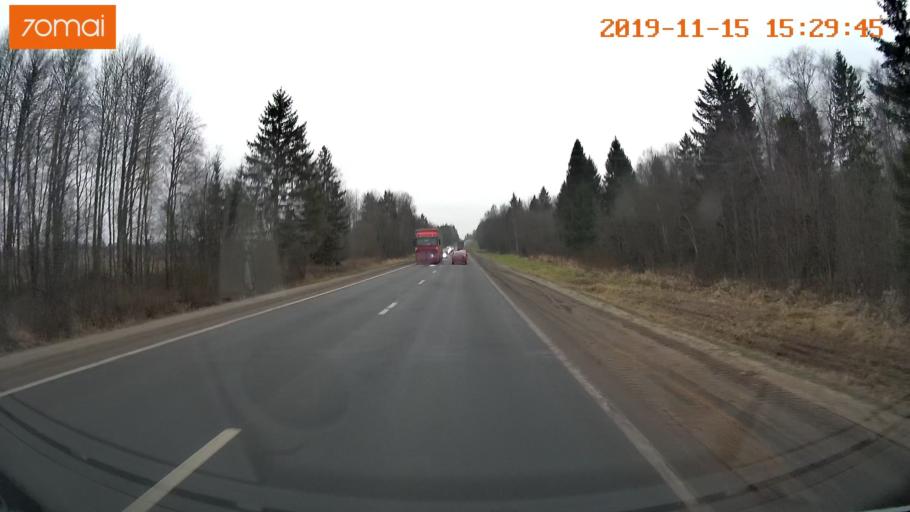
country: RU
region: Jaroslavl
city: Danilov
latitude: 58.1172
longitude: 40.1174
